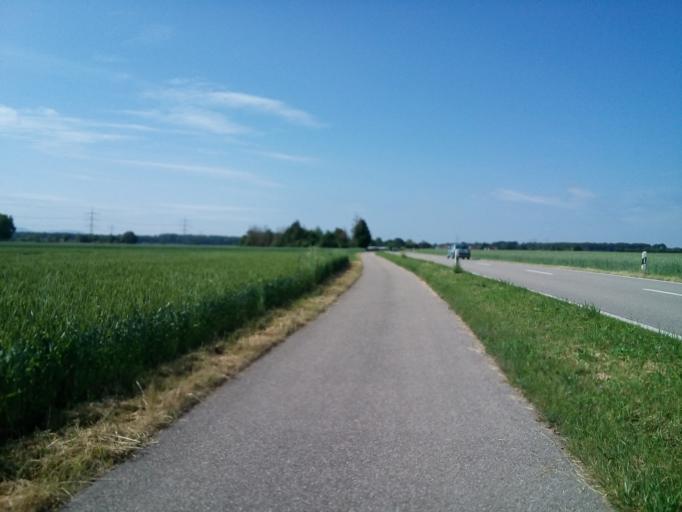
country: DE
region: Baden-Wuerttemberg
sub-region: Freiburg Region
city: Rheinau
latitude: 48.6392
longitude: 7.9241
